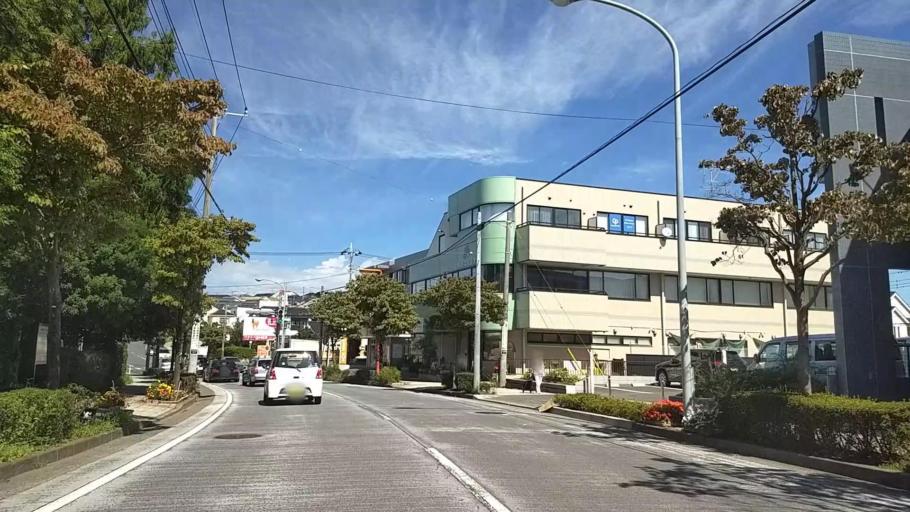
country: JP
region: Tokyo
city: Chofugaoka
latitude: 35.5615
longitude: 139.5503
